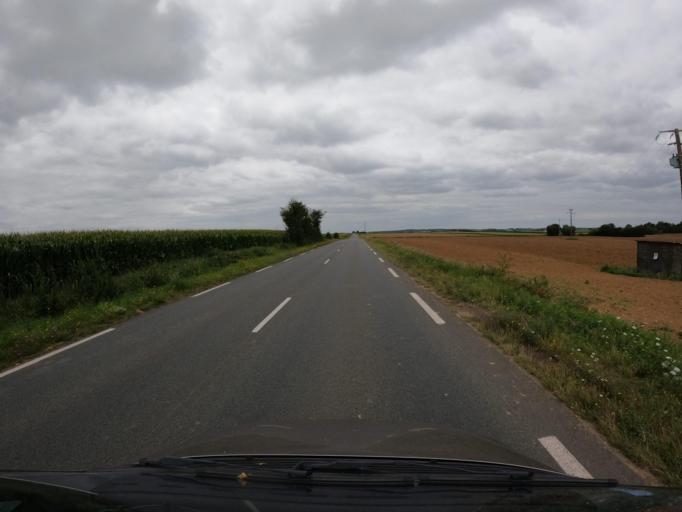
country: FR
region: Pays de la Loire
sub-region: Departement de la Vendee
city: Sainte-Hermine
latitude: 46.5381
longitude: -1.0200
